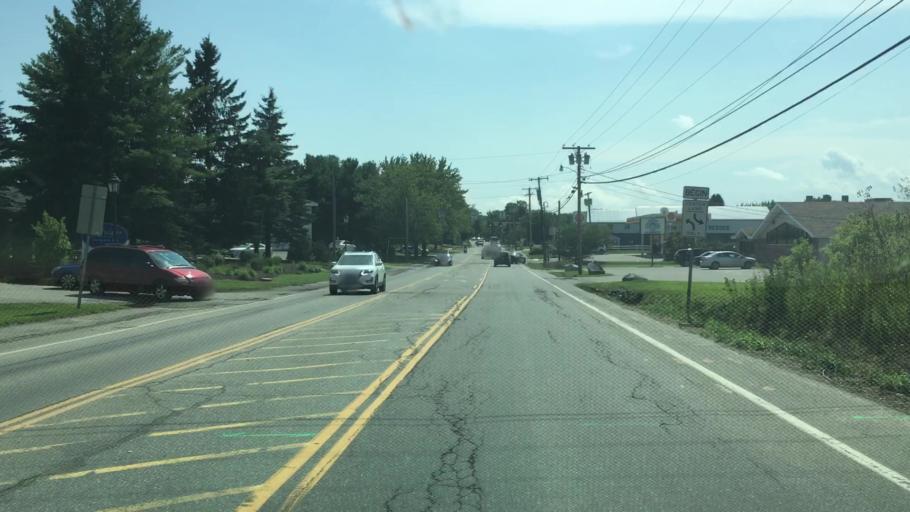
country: US
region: Maine
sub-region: Penobscot County
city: Brewer
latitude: 44.8230
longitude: -68.7599
